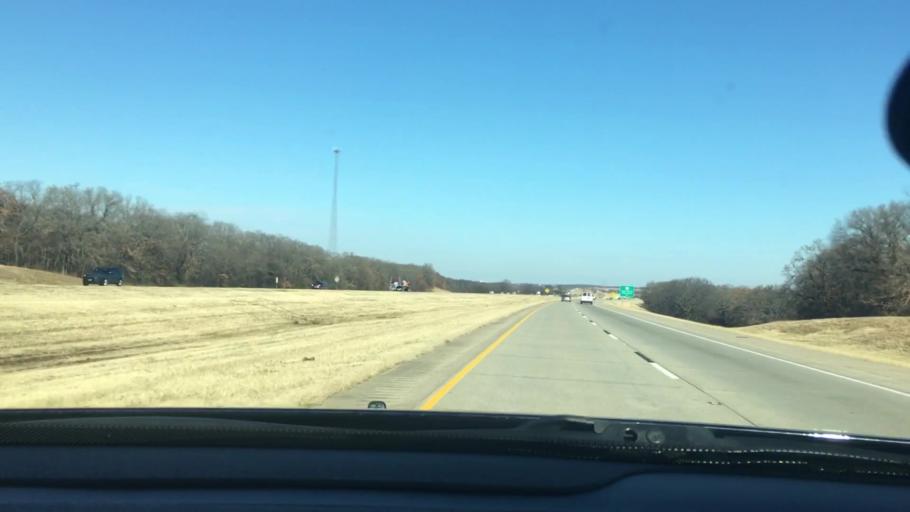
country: US
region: Oklahoma
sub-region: Carter County
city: Ardmore
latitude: 34.0631
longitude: -97.1494
